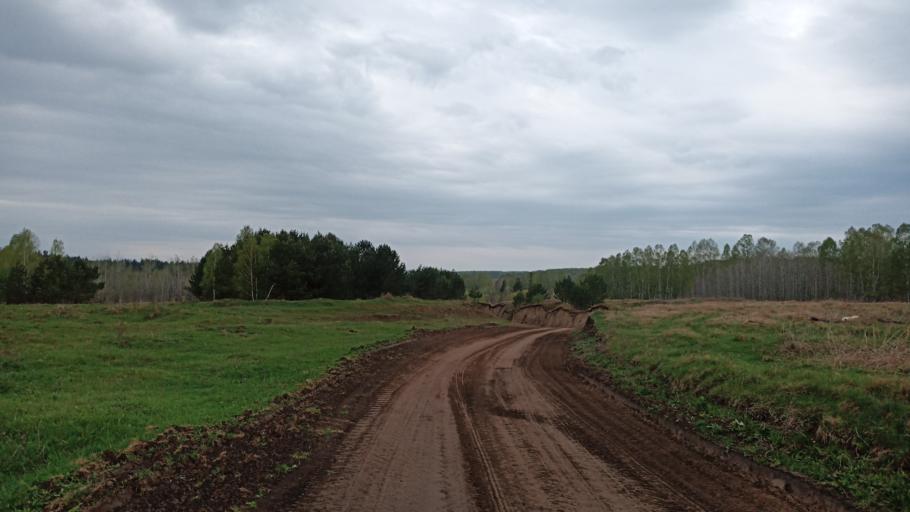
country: RU
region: Altai Krai
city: Bayunovskiye Klyuchi
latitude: 53.2449
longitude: 84.3496
